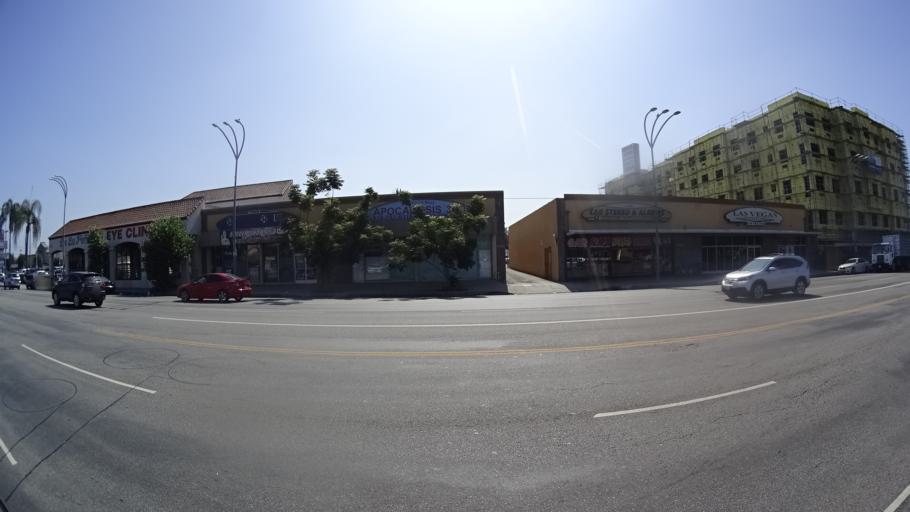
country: US
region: California
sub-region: Los Angeles County
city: Van Nuys
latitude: 34.1992
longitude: -118.4489
